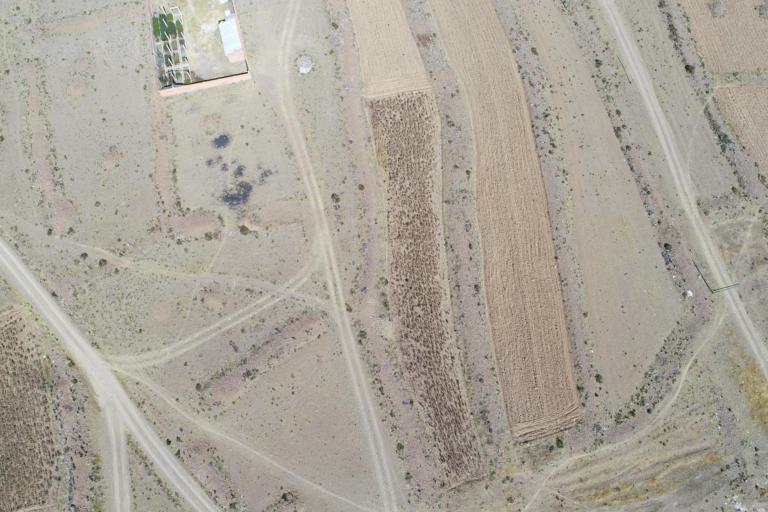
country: BO
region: La Paz
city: Achacachi
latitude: -15.9016
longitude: -68.9066
